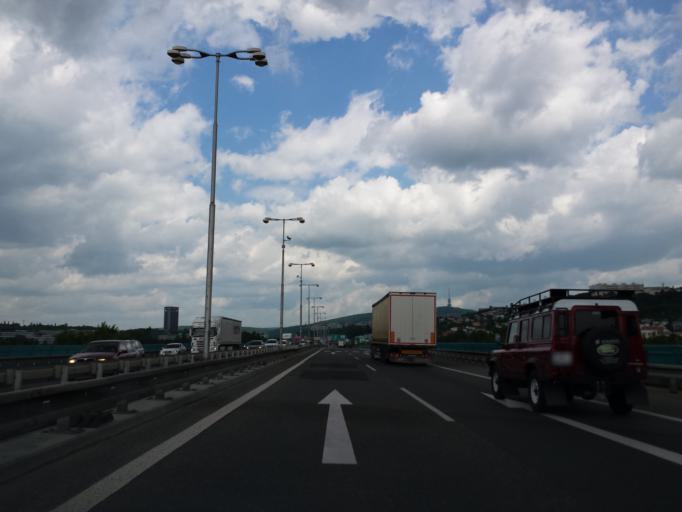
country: SK
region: Bratislavsky
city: Bratislava
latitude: 48.1401
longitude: 17.0750
